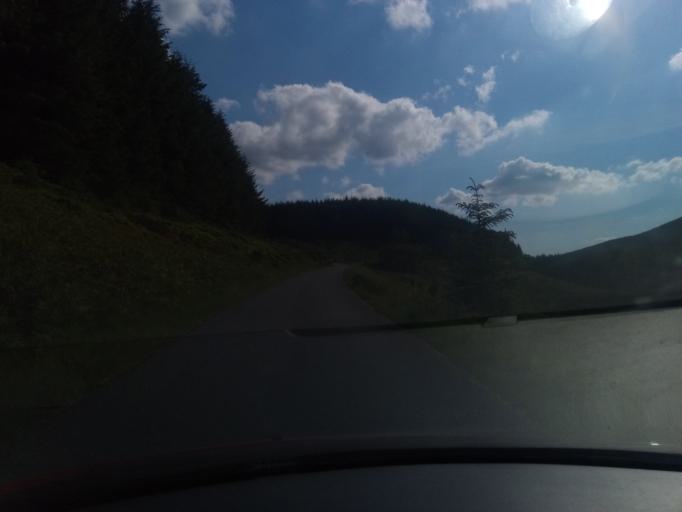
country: GB
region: Scotland
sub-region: The Scottish Borders
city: Innerleithen
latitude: 55.4710
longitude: -3.1459
